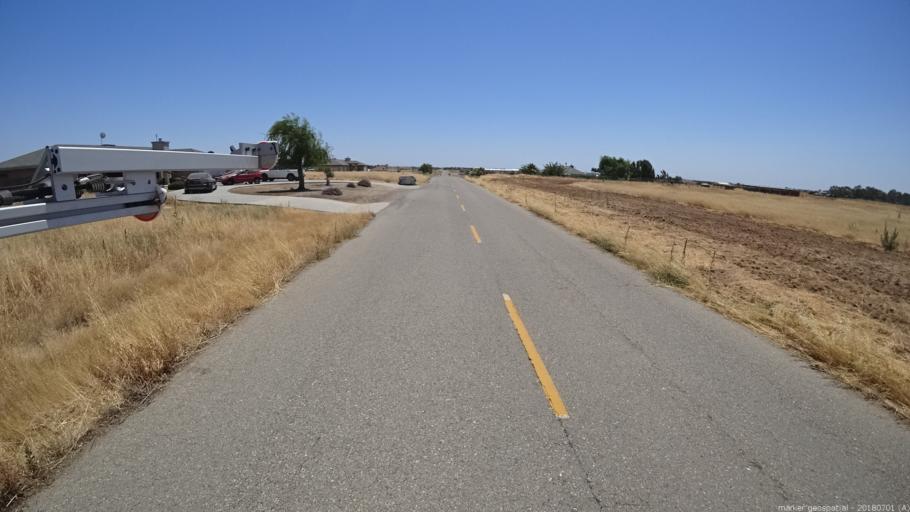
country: US
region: California
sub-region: Madera County
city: Madera Acres
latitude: 37.0640
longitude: -120.0112
